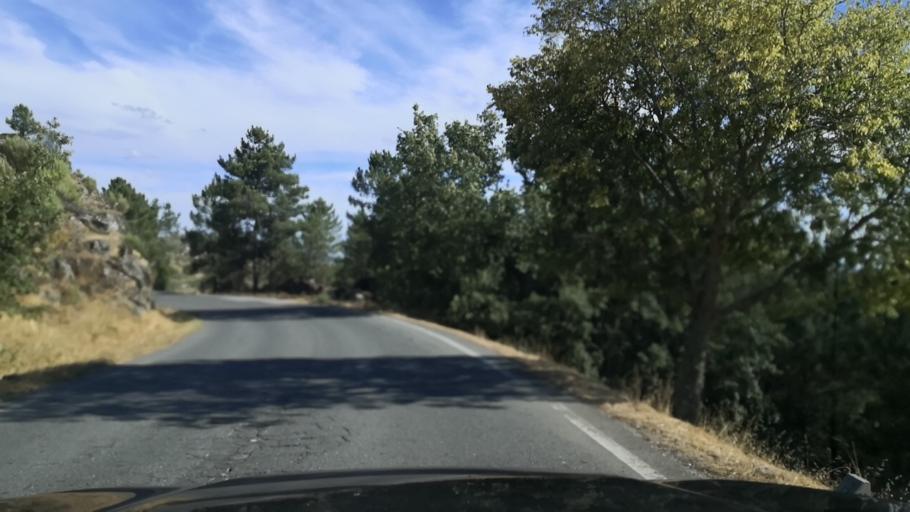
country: PT
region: Vila Real
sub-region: Murca
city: Murca
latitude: 41.3706
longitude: -7.5418
